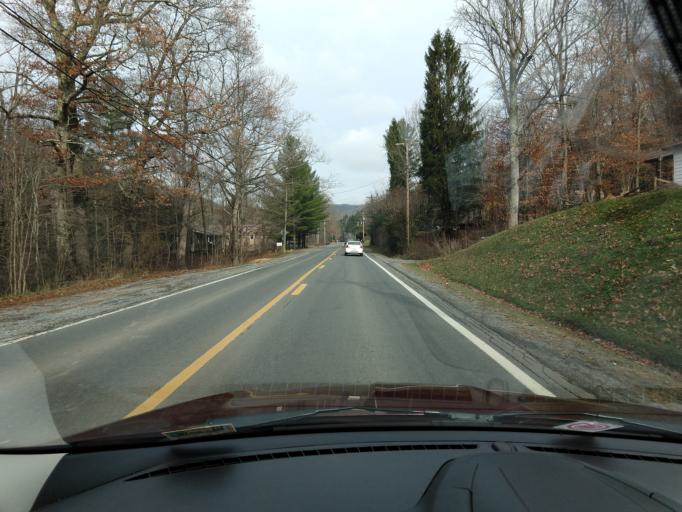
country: US
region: West Virginia
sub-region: Greenbrier County
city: Rainelle
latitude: 37.9915
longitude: -80.7326
